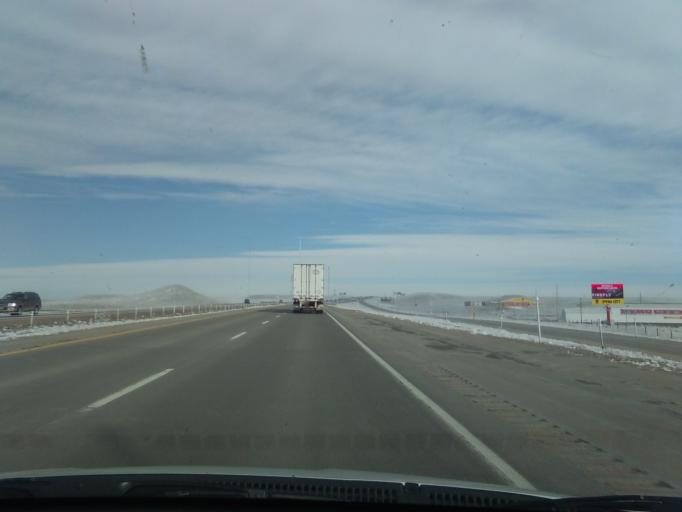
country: US
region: Wyoming
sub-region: Laramie County
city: South Greeley
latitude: 41.0329
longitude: -104.8980
